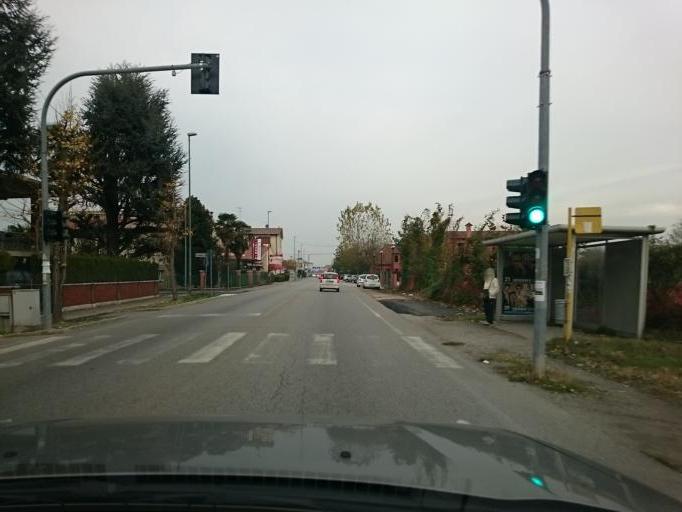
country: IT
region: Veneto
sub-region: Provincia di Padova
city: Caselle
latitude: 45.4136
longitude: 11.8258
